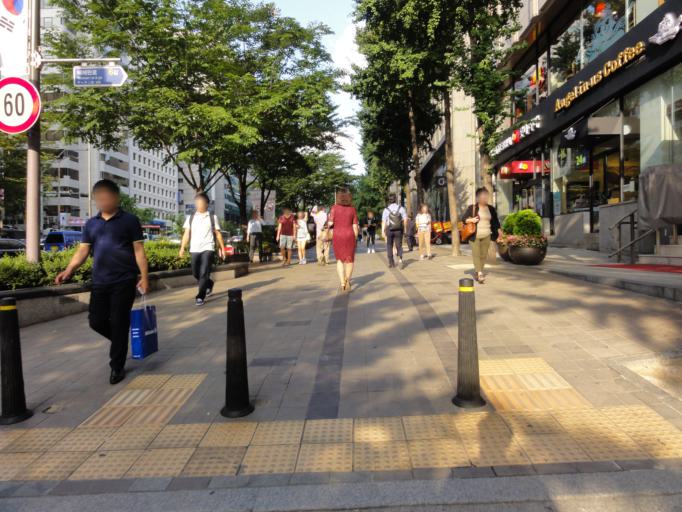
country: KR
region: Seoul
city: Seoul
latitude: 37.4988
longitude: 127.0306
